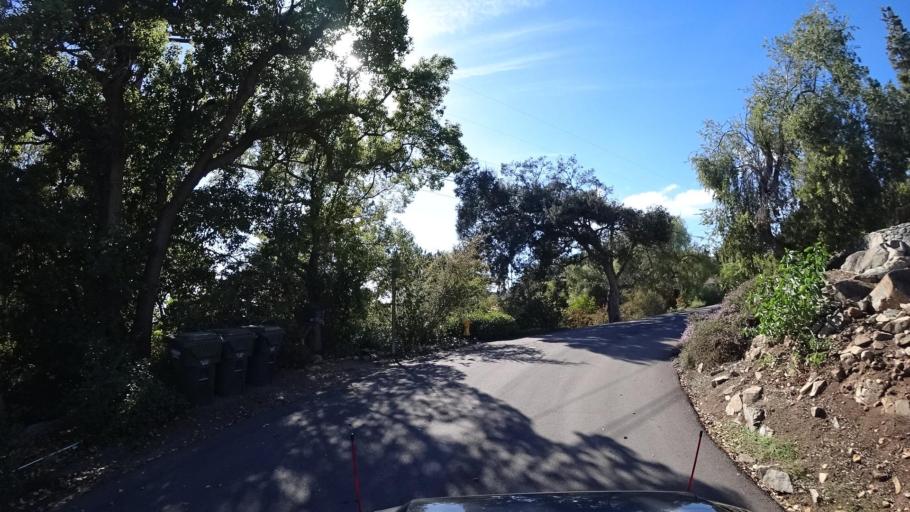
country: US
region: California
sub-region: San Diego County
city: Casa de Oro-Mount Helix
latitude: 32.7599
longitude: -116.9552
